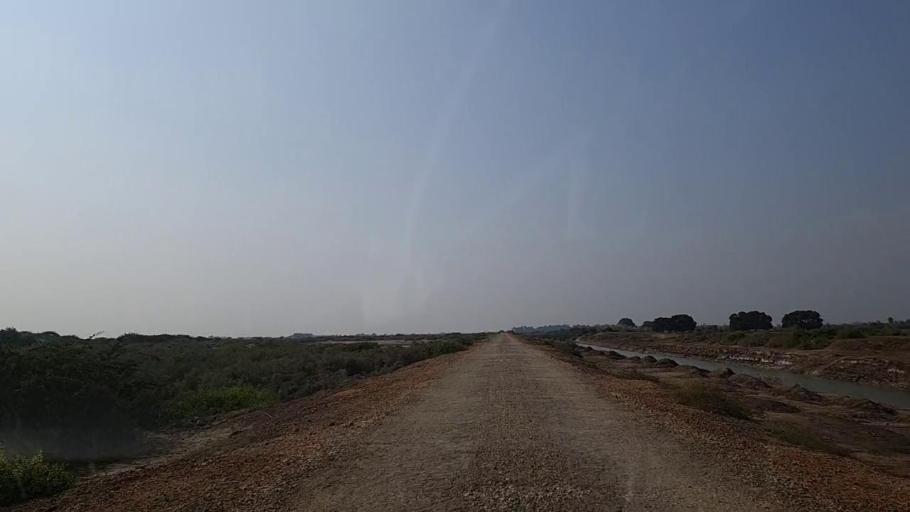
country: PK
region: Sindh
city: Mirpur Sakro
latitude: 24.6346
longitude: 67.7104
